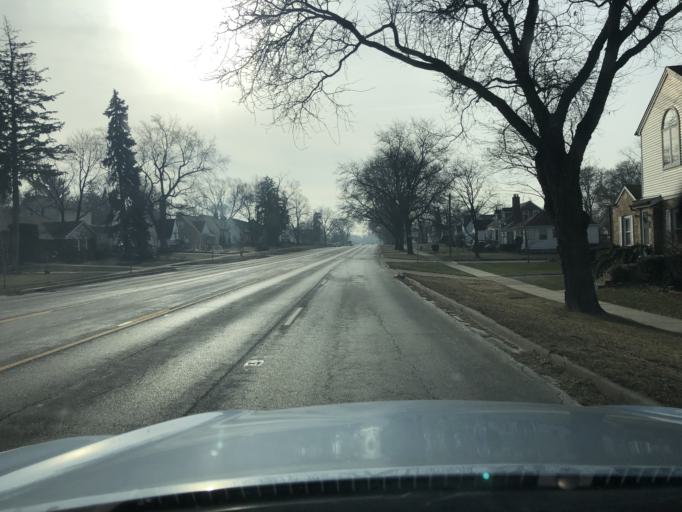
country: US
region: Illinois
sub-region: Cook County
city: Mount Prospect
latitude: 42.0484
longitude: -87.9121
